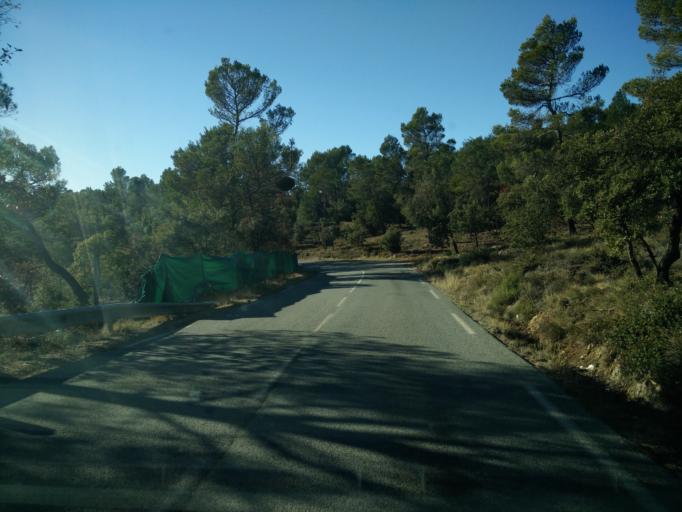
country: FR
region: Provence-Alpes-Cote d'Azur
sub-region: Departement du Var
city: Aups
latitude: 43.5967
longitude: 6.2214
